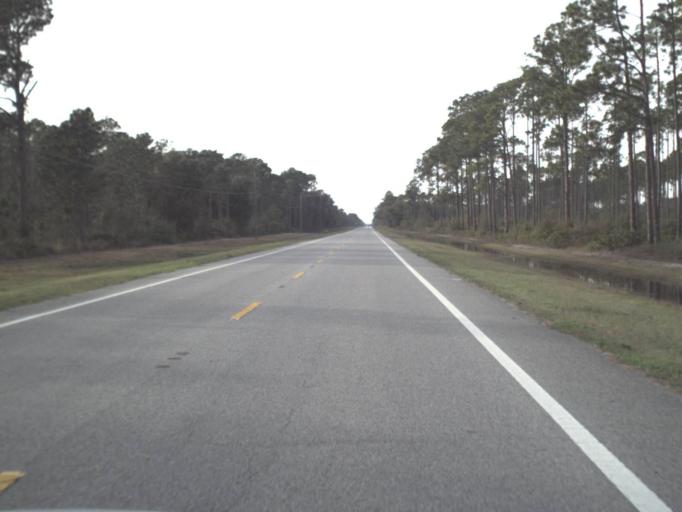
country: US
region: Florida
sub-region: Bay County
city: Tyndall Air Force Base
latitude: 30.0369
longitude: -85.5472
